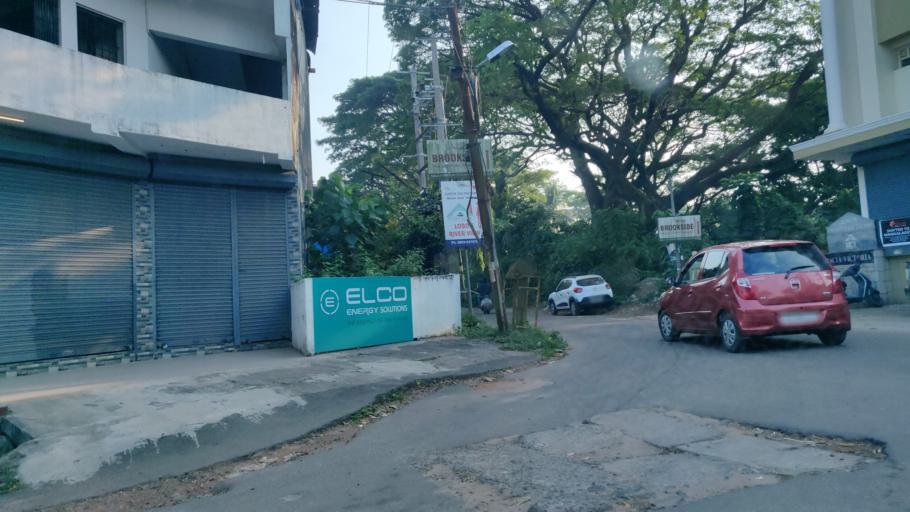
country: IN
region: Karnataka
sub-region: Dakshina Kannada
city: Ullal
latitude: 12.8479
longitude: 74.8526
